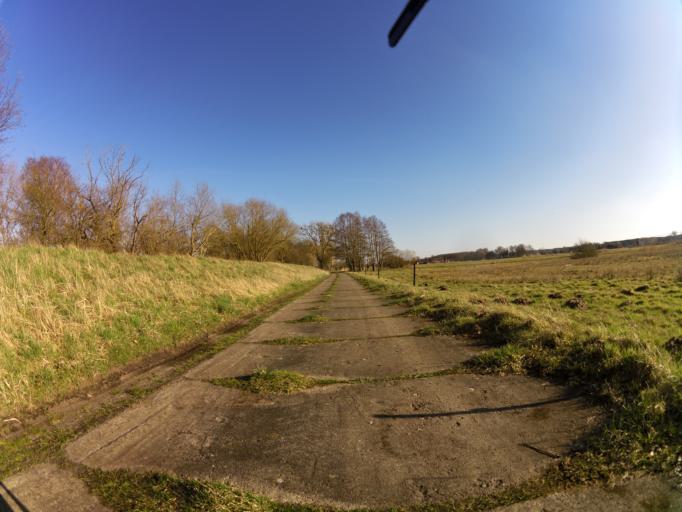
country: PL
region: West Pomeranian Voivodeship
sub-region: Powiat policki
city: Nowe Warpno
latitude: 53.7030
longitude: 14.3611
